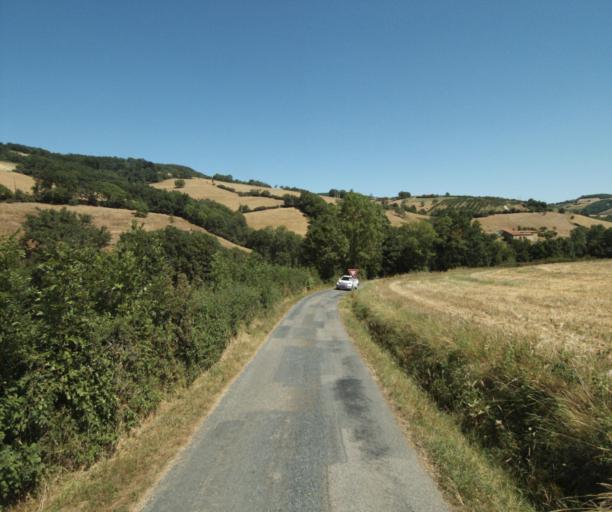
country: FR
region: Rhone-Alpes
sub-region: Departement du Rhone
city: Montrottier
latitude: 45.7883
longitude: 4.5050
